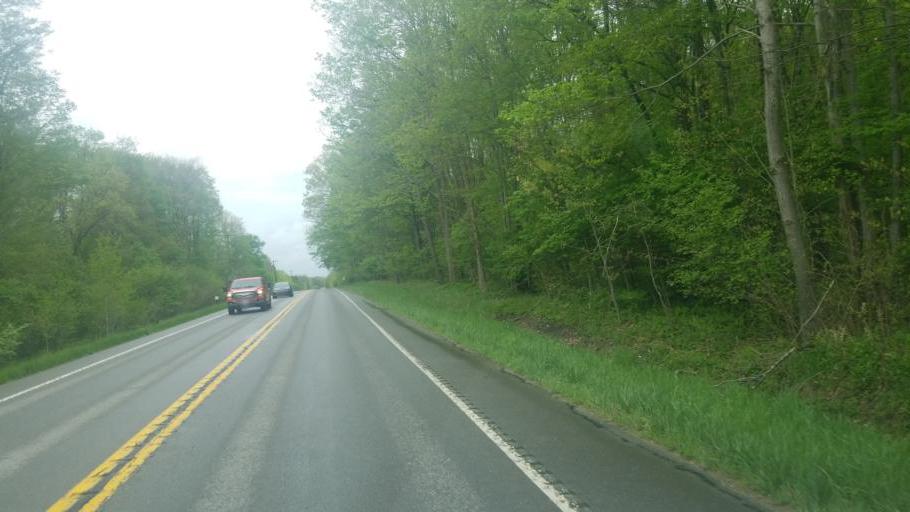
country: US
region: Pennsylvania
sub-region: Forest County
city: Marienville
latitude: 41.4298
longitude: -79.1915
